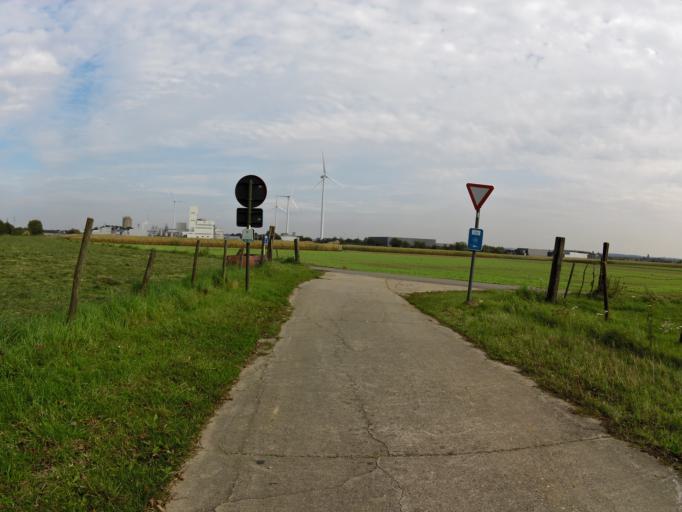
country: BE
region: Flanders
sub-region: Provincie Limburg
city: Lanaken
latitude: 50.8742
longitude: 5.6436
